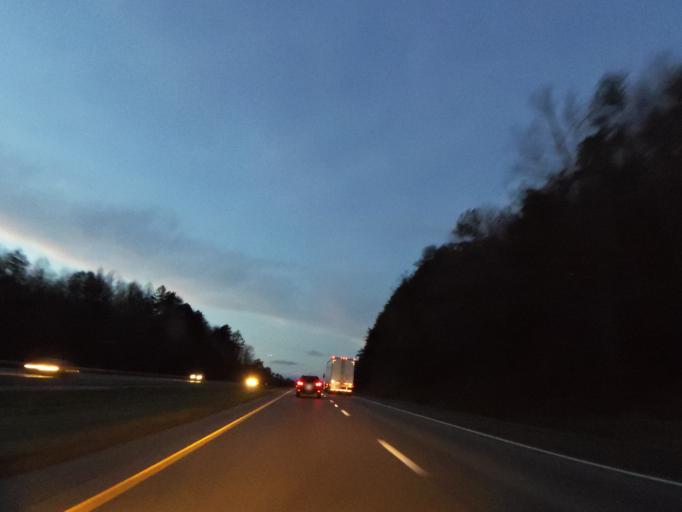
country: US
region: Kentucky
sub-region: Whitley County
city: Corbin
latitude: 36.8754
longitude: -84.1490
